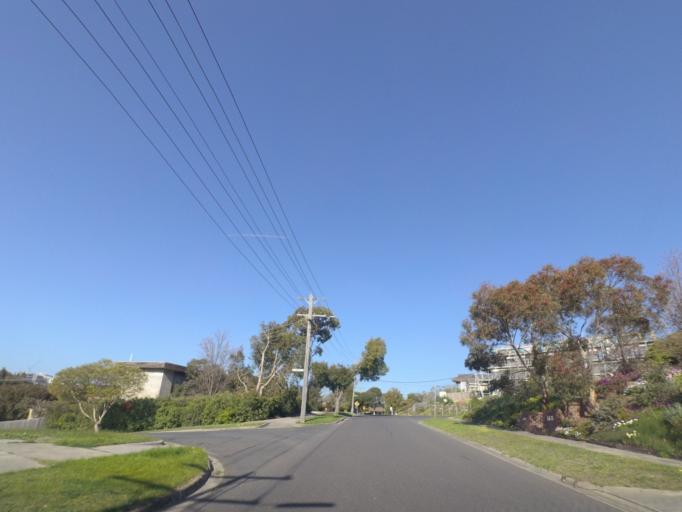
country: AU
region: Victoria
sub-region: Whitehorse
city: Mont Albert North
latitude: -37.7933
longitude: 145.1052
